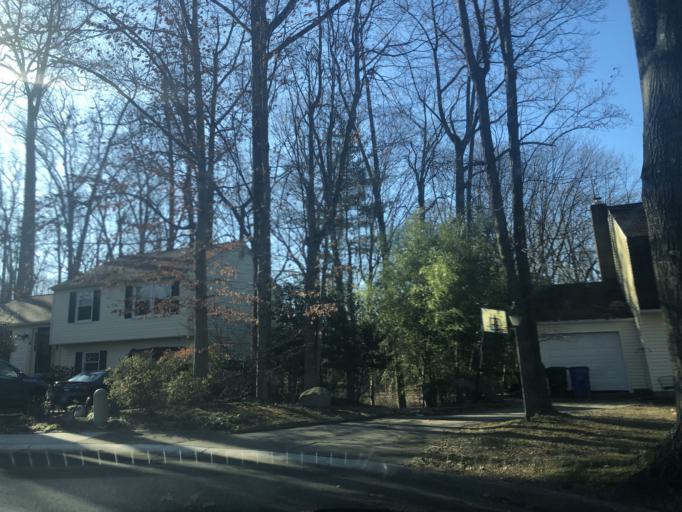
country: US
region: Maryland
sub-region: Howard County
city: Columbia
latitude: 39.2021
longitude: -76.8307
